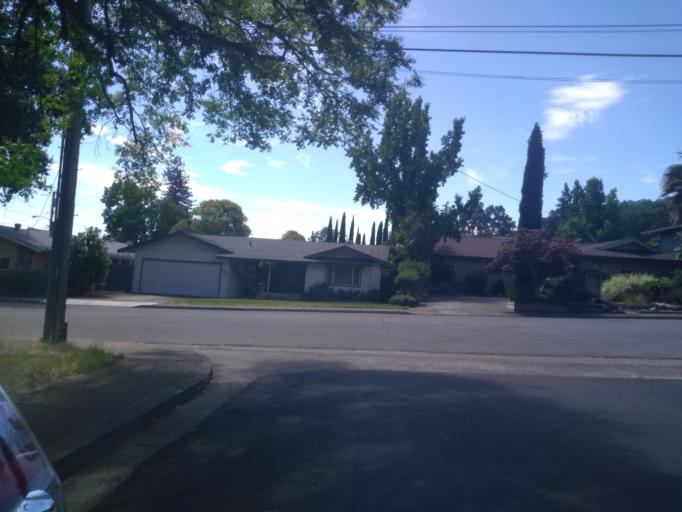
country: US
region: California
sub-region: Mendocino County
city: Ukiah
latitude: 39.1464
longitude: -123.2184
